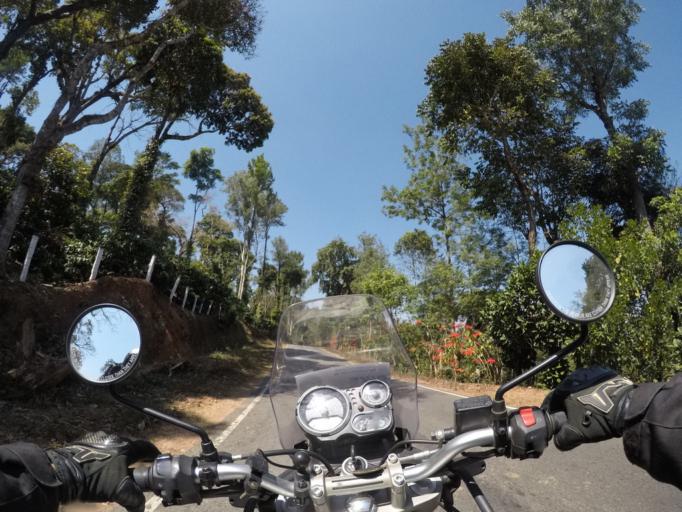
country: IN
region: Karnataka
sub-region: Hassan
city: Sakleshpur
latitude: 13.0129
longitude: 75.6994
